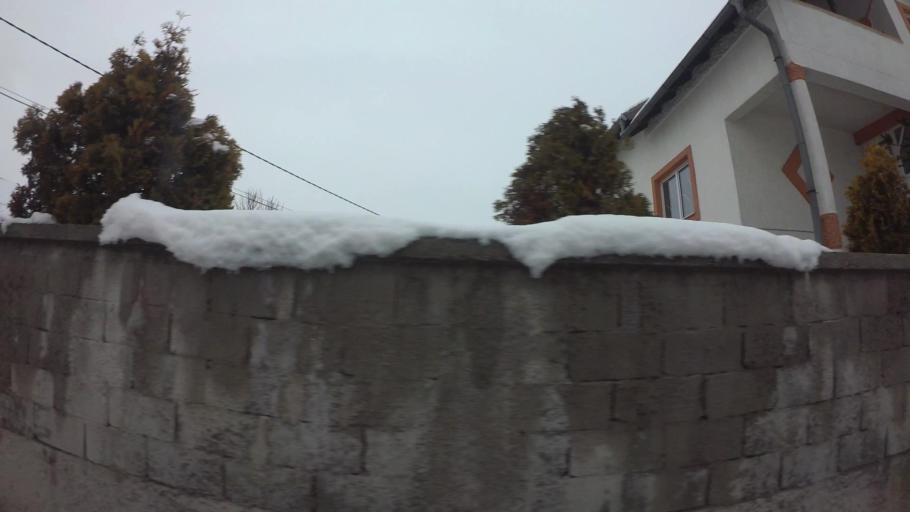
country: BA
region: Federation of Bosnia and Herzegovina
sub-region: Kanton Sarajevo
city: Sarajevo
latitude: 43.8403
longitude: 18.3102
